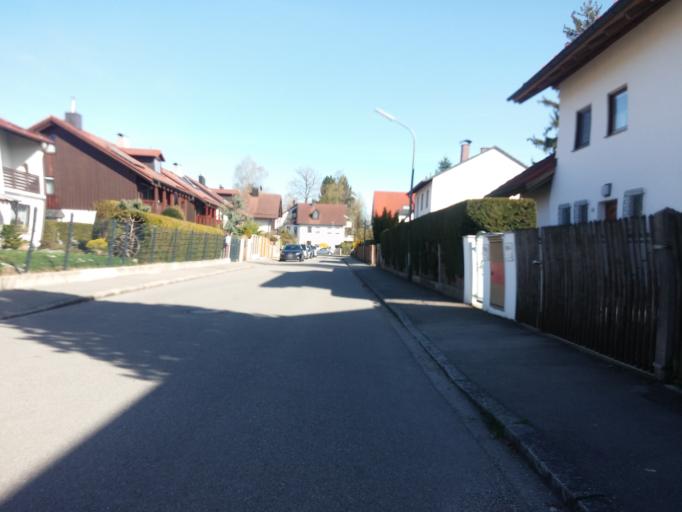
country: DE
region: Bavaria
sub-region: Upper Bavaria
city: Neubiberg
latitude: 48.0811
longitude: 11.6638
